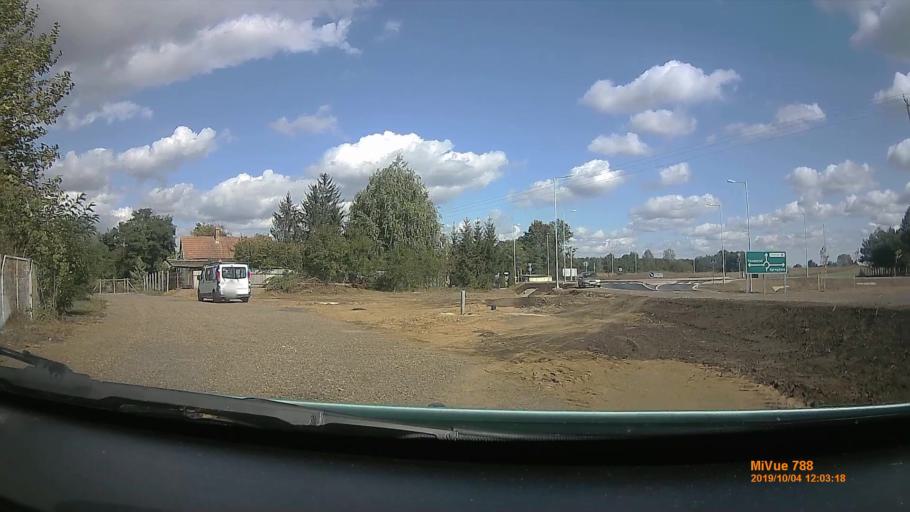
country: HU
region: Szabolcs-Szatmar-Bereg
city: Kotaj
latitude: 48.0230
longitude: 21.6798
